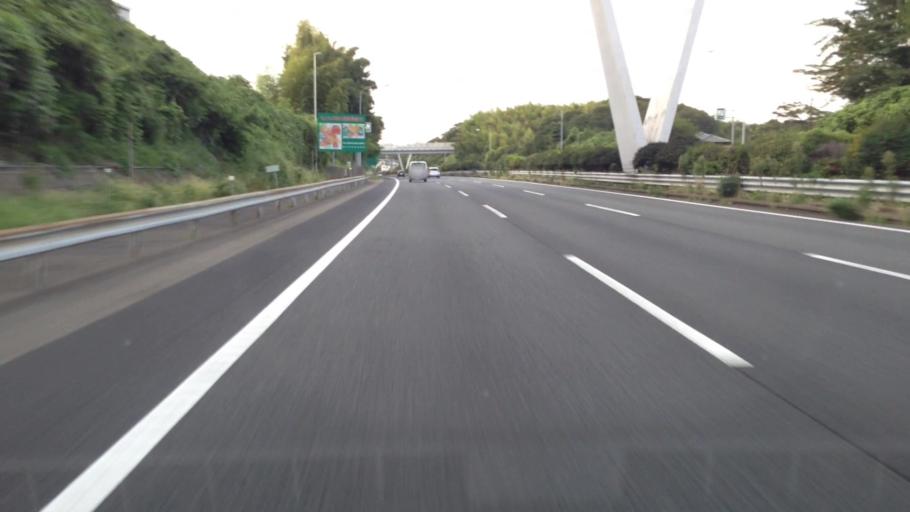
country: JP
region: Kanagawa
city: Yokohama
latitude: 35.5035
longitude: 139.5923
